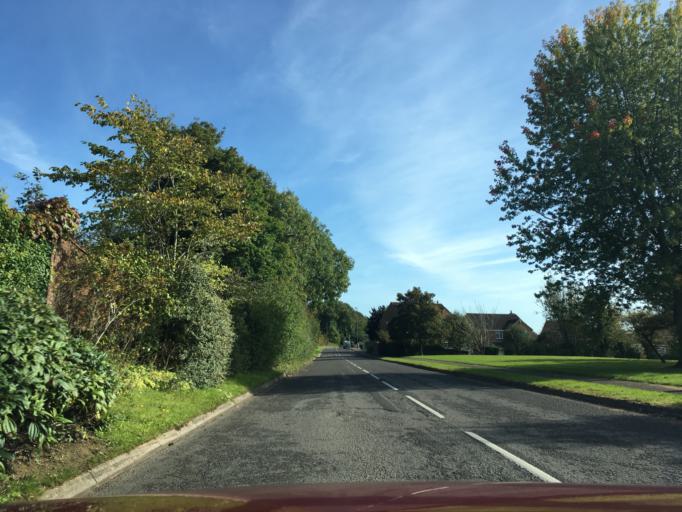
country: GB
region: England
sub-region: South Gloucestershire
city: Chipping Sodbury
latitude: 51.5512
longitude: -2.4047
